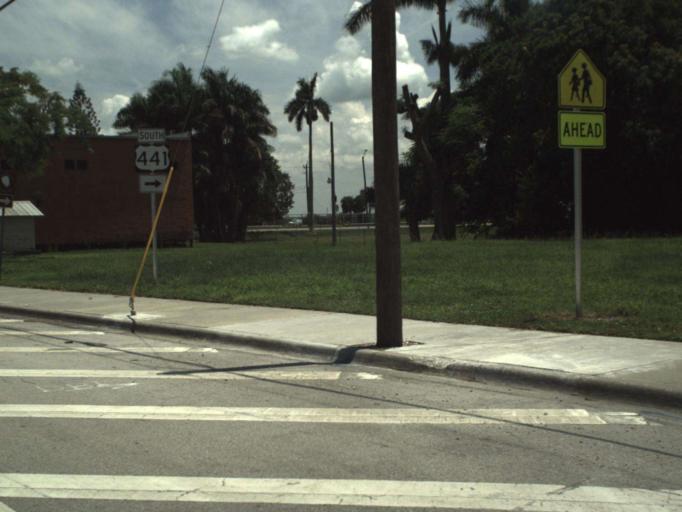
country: US
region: Florida
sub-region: Palm Beach County
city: Pahokee
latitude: 26.8625
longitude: -80.6319
